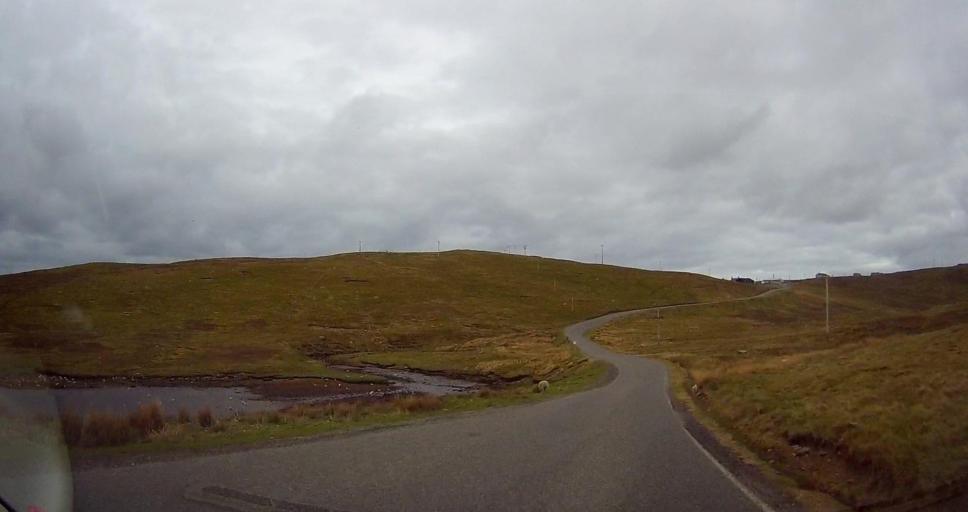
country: GB
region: Scotland
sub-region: Shetland Islands
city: Shetland
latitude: 60.6033
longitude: -1.0849
